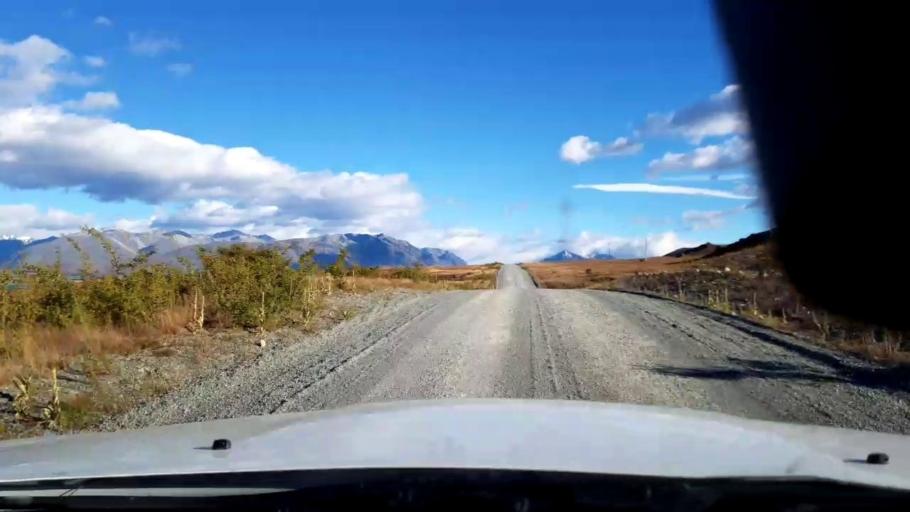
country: NZ
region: Canterbury
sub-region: Timaru District
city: Pleasant Point
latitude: -43.9249
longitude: 170.5601
